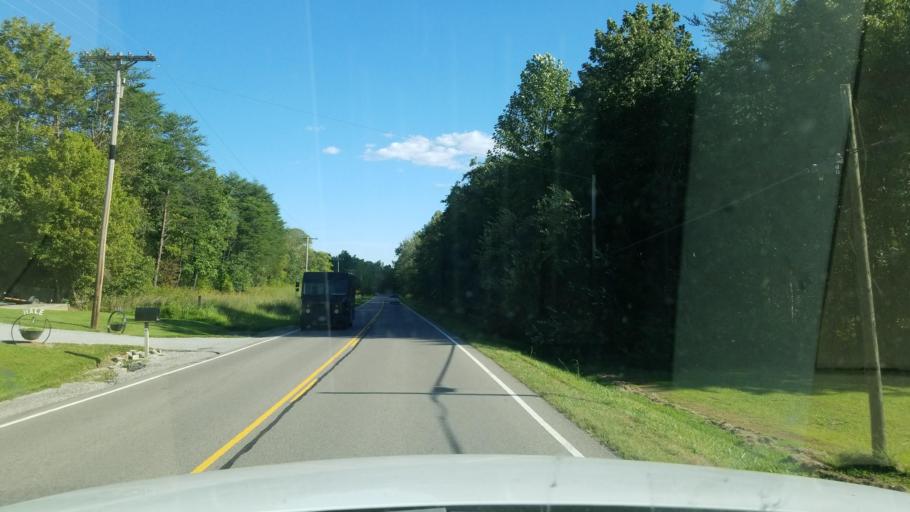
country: US
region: Illinois
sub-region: Saline County
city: Harrisburg
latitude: 37.6059
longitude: -88.4619
